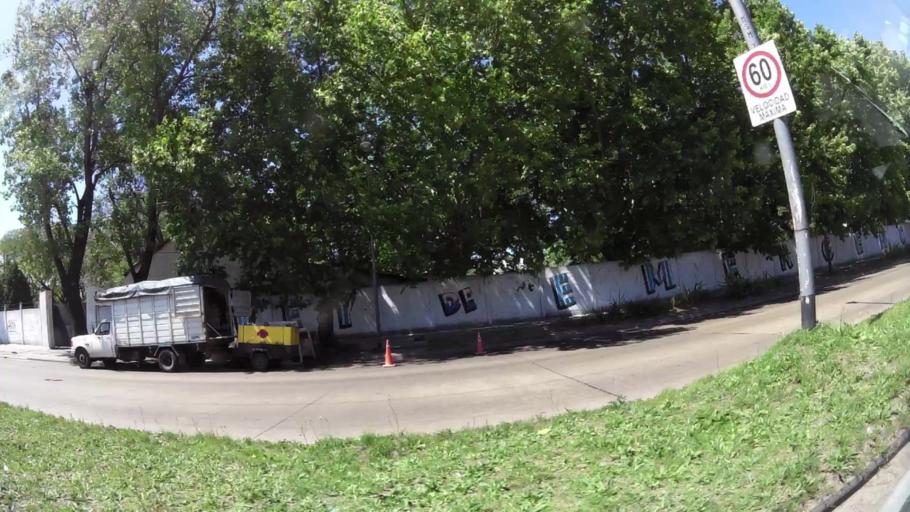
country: AR
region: Buenos Aires
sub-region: Partido de General San Martin
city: General San Martin
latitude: -34.5701
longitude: -58.5550
